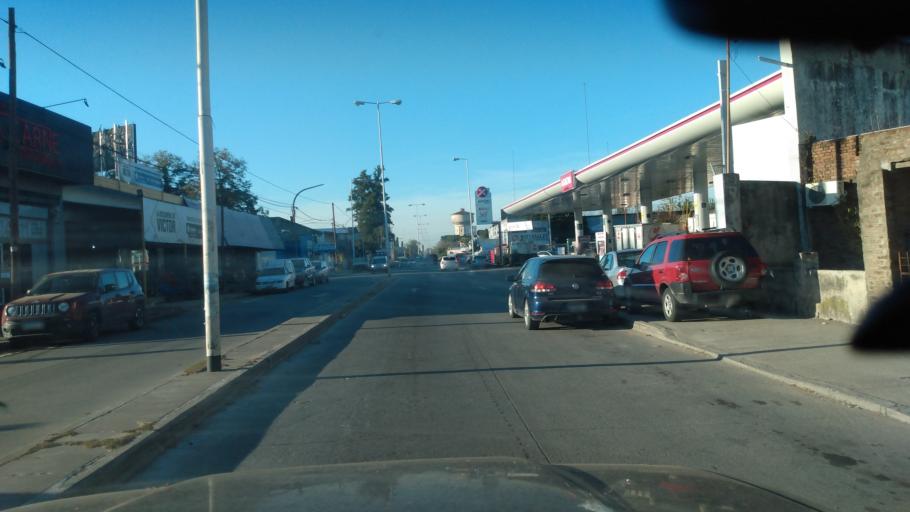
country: AR
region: Buenos Aires
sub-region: Partido de Lujan
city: Lujan
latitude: -34.5684
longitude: -59.0953
